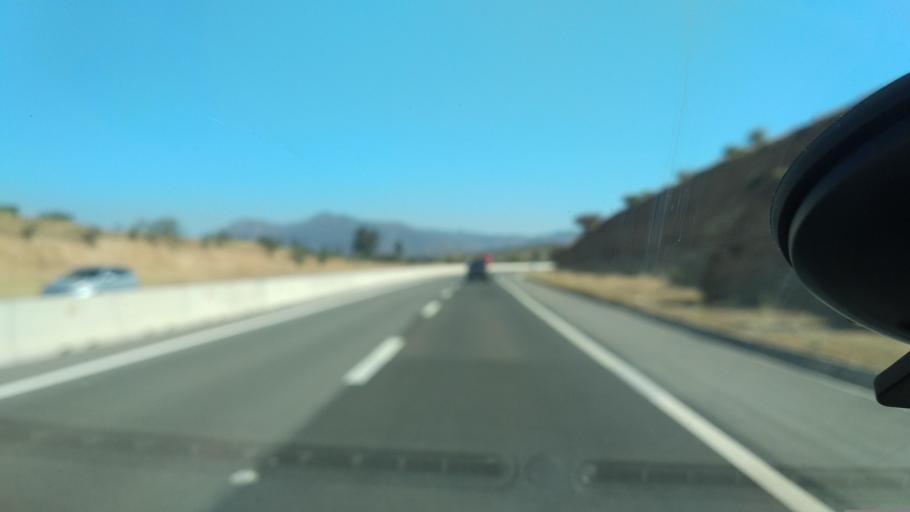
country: CL
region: Valparaiso
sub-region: Provincia de Marga Marga
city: Villa Alemana
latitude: -32.9999
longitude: -71.3291
